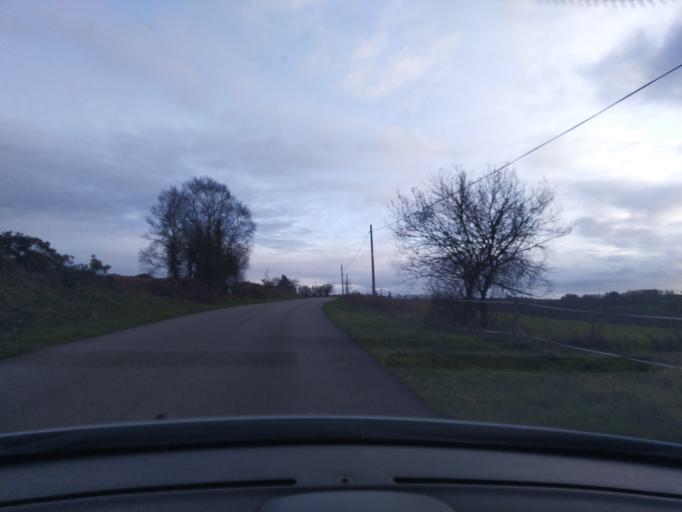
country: FR
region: Brittany
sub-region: Departement du Finistere
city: Guerlesquin
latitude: 48.5263
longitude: -3.6036
